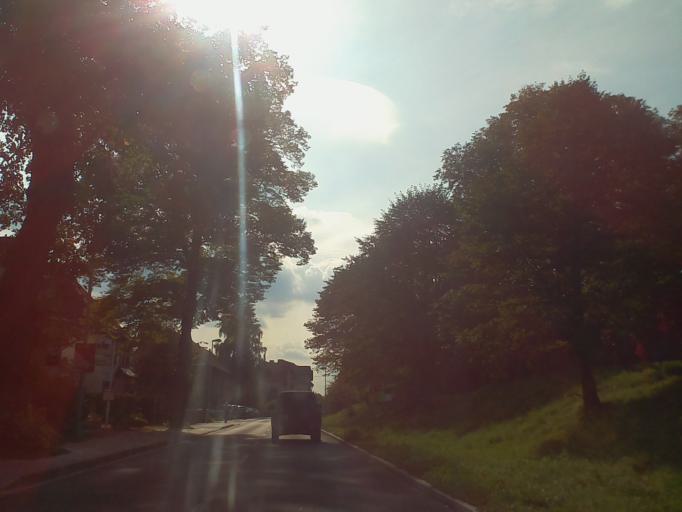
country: DE
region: Thuringia
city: Gerstungen
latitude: 50.9596
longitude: 10.0597
